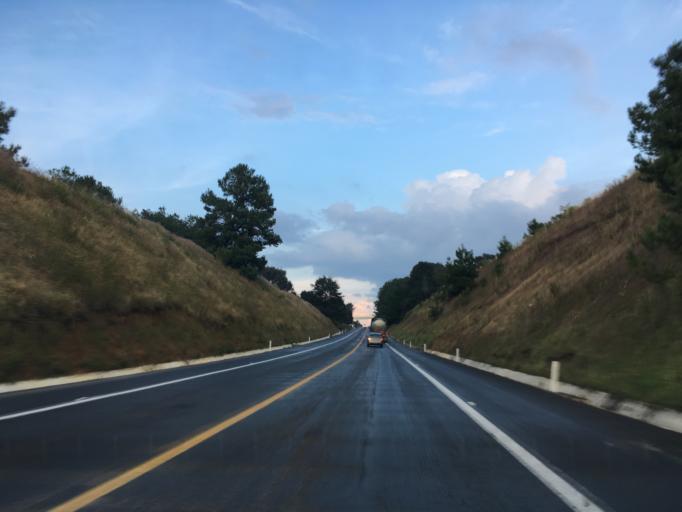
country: MX
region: Michoacan
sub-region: Patzcuaro
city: Santa Maria Huiramangaro (San Juan Tumbio)
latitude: 19.4925
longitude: -101.7059
